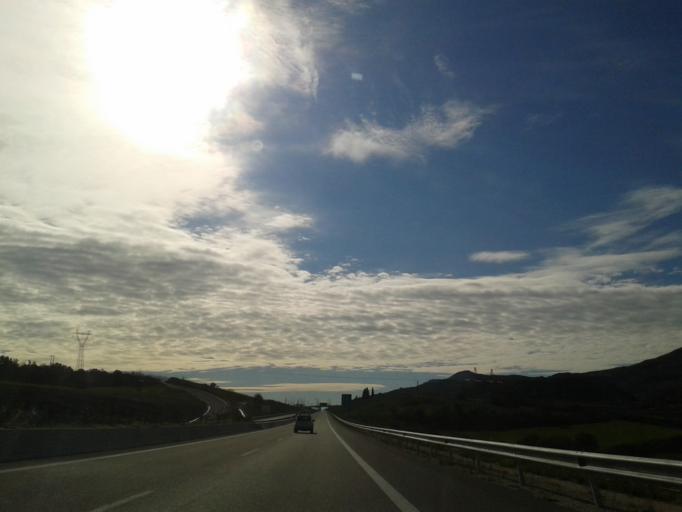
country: GR
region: West Greece
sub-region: Nomos Aitolias kai Akarnanias
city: Fitiai
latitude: 38.7101
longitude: 21.2092
